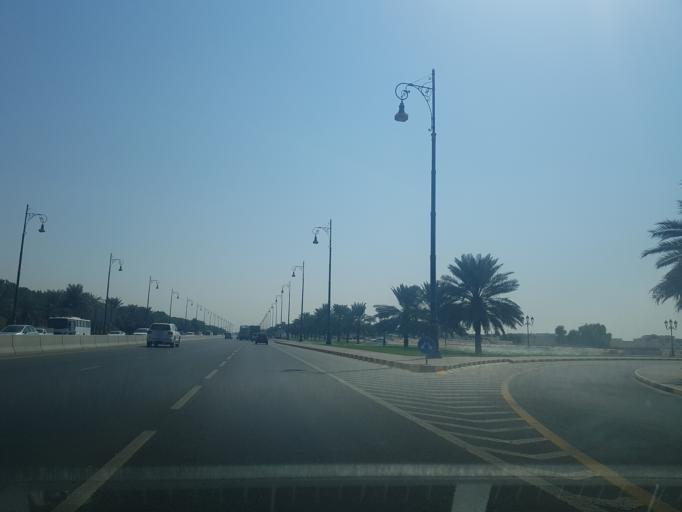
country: AE
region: Ash Shariqah
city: Sharjah
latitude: 25.3208
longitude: 55.5049
